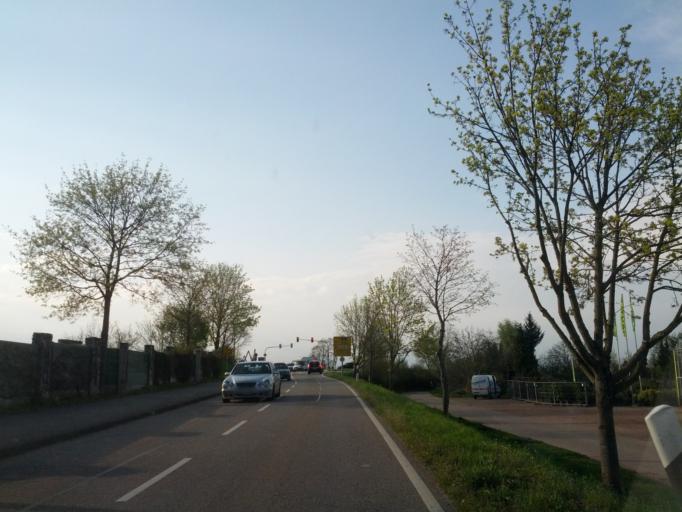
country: DE
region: Baden-Wuerttemberg
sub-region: Freiburg Region
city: Gundelfingen
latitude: 48.0488
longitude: 7.8615
